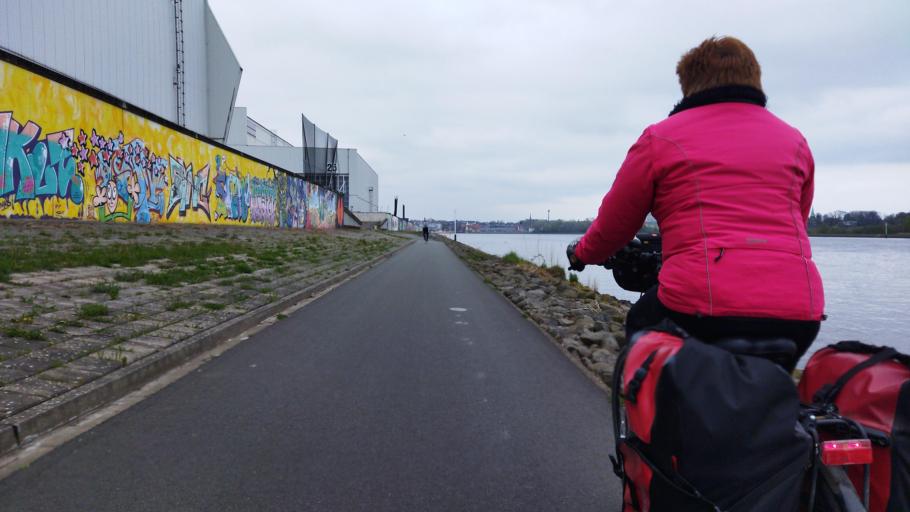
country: DE
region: Lower Saxony
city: Lemwerder
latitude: 53.1541
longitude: 8.6246
